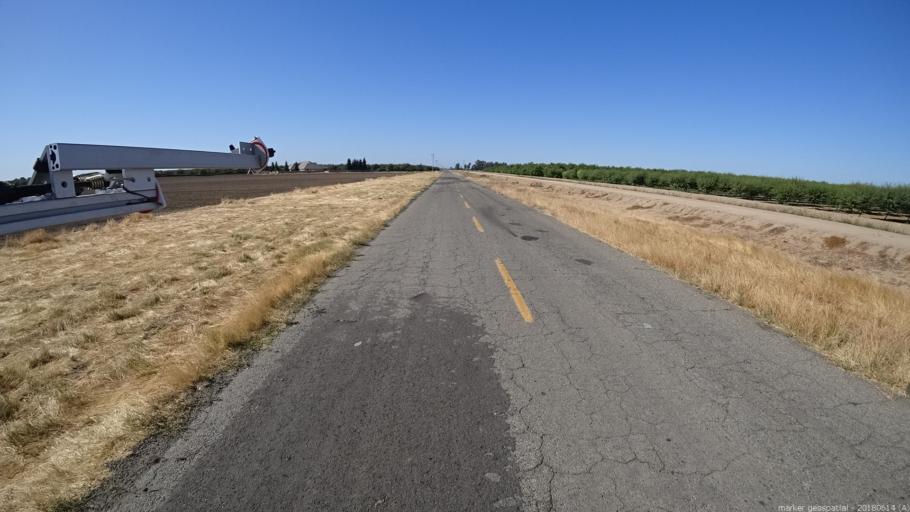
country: US
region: California
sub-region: Madera County
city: Fairmead
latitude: 37.0066
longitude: -120.1661
